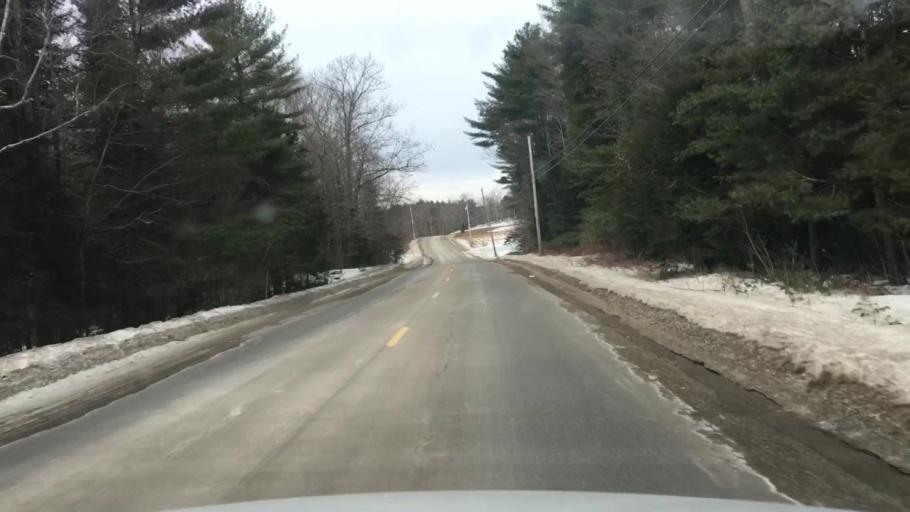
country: US
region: Maine
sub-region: Kennebec County
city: Chelsea
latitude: 44.2641
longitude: -69.6483
